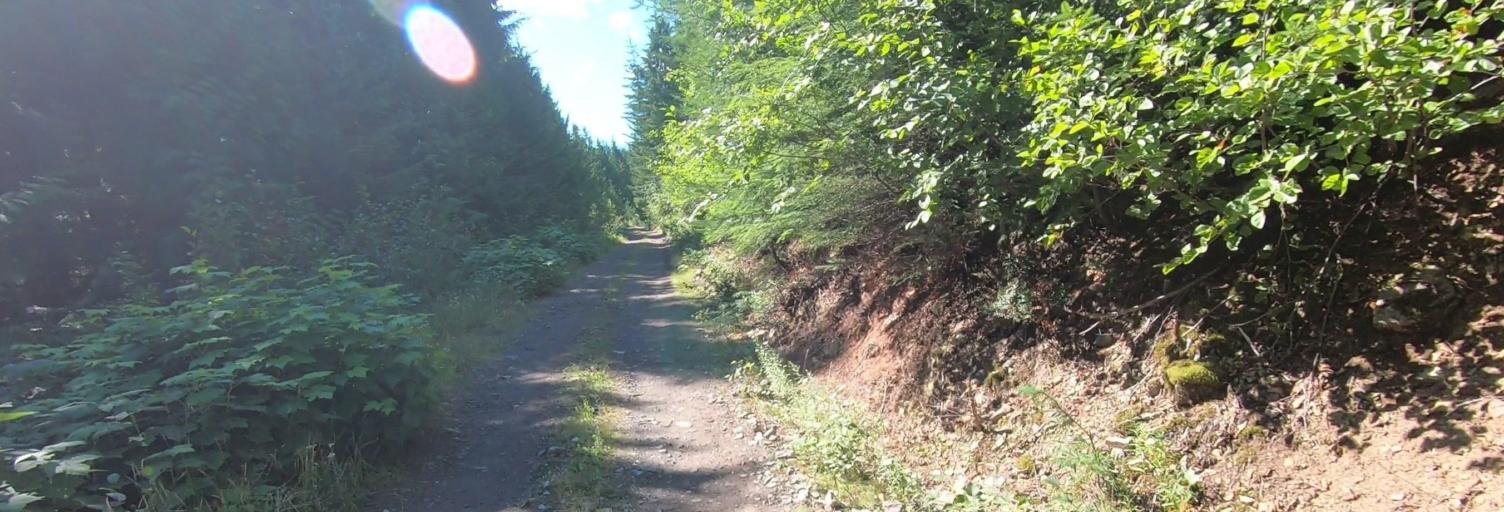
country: CA
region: British Columbia
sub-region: Fraser Valley Regional District
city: Chilliwack
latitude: 48.8604
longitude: -121.7795
